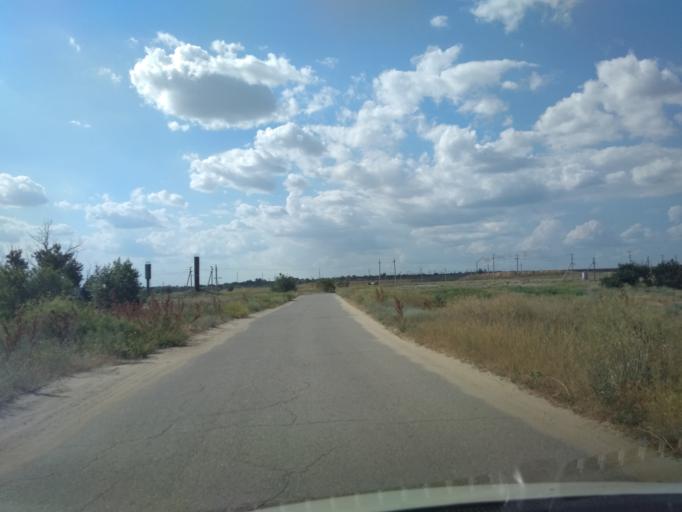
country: RU
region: Volgograd
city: Vodstroy
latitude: 48.8038
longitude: 44.5299
